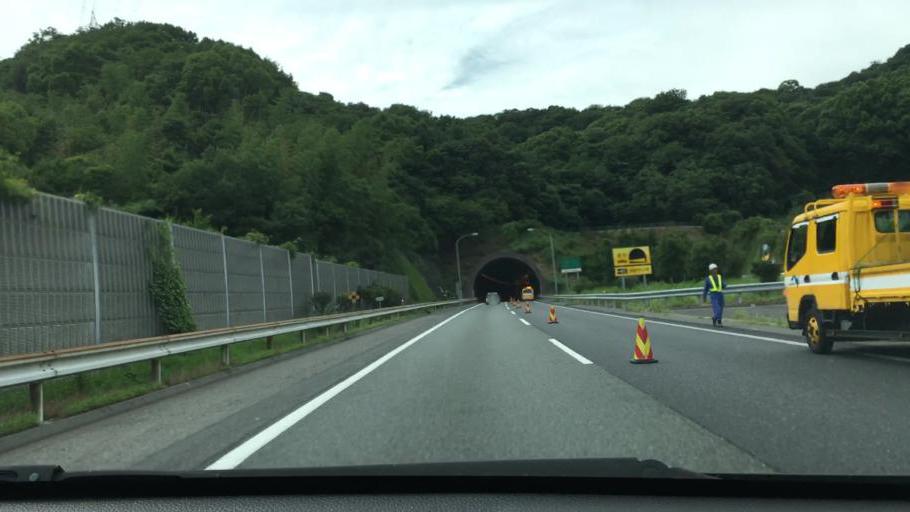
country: JP
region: Yamaguchi
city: Tokuyama
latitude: 34.0517
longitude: 131.8433
